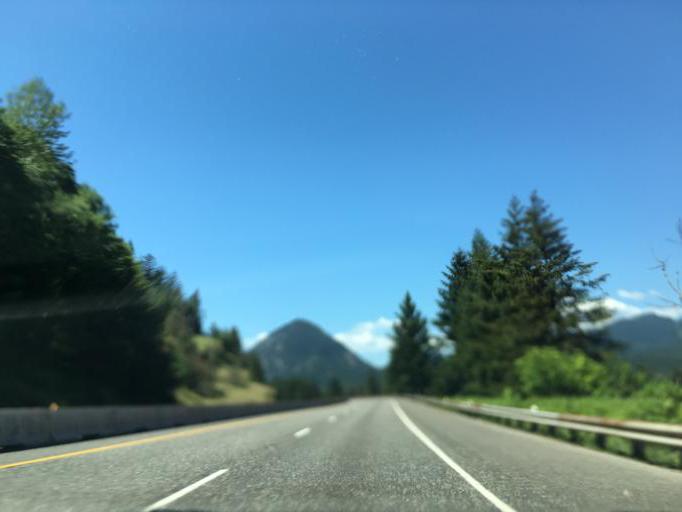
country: US
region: Washington
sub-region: Skamania County
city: Carson
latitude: 45.6885
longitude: -121.7157
